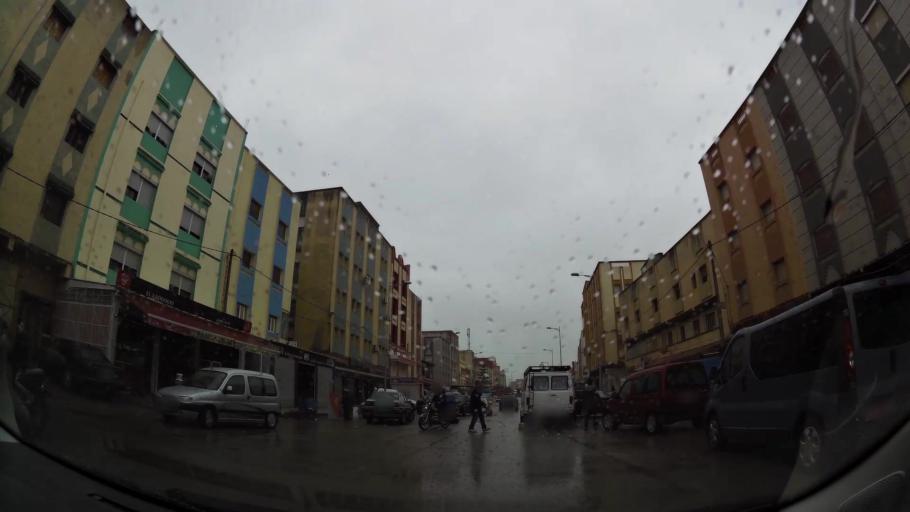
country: MA
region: Oriental
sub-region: Nador
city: Boudinar
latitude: 35.1179
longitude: -3.6410
